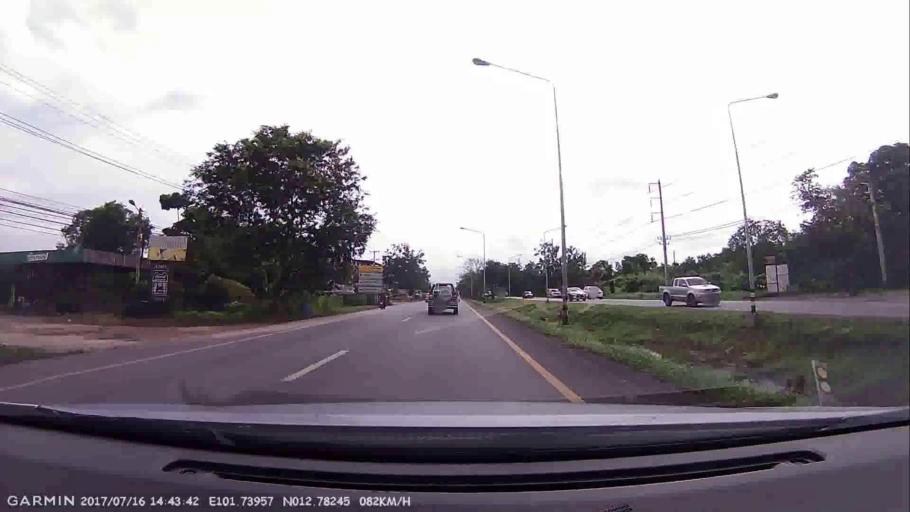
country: TH
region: Chanthaburi
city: Na Yai Am
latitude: 12.7824
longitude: 101.7394
